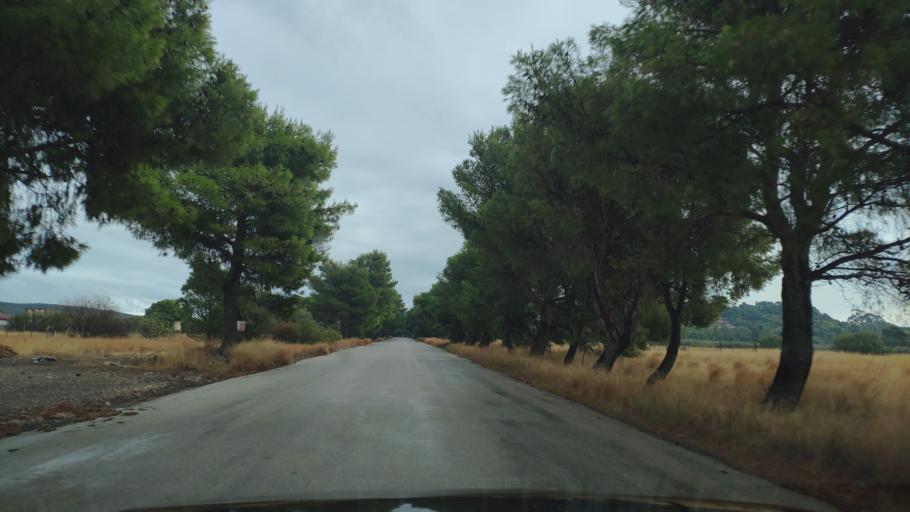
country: GR
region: Peloponnese
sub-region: Nomos Korinthias
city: Loutraki
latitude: 37.9651
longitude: 22.9922
